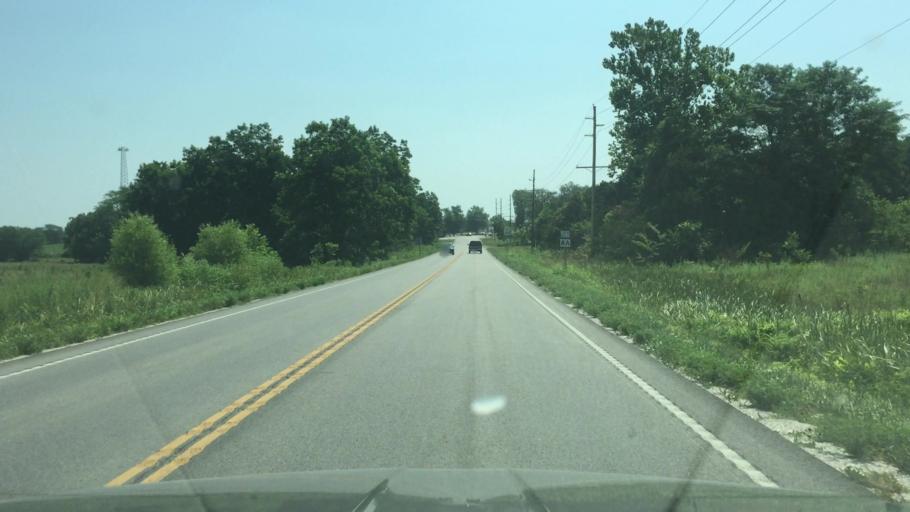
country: US
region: Missouri
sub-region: Miller County
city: Eldon
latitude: 38.3813
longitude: -92.6789
